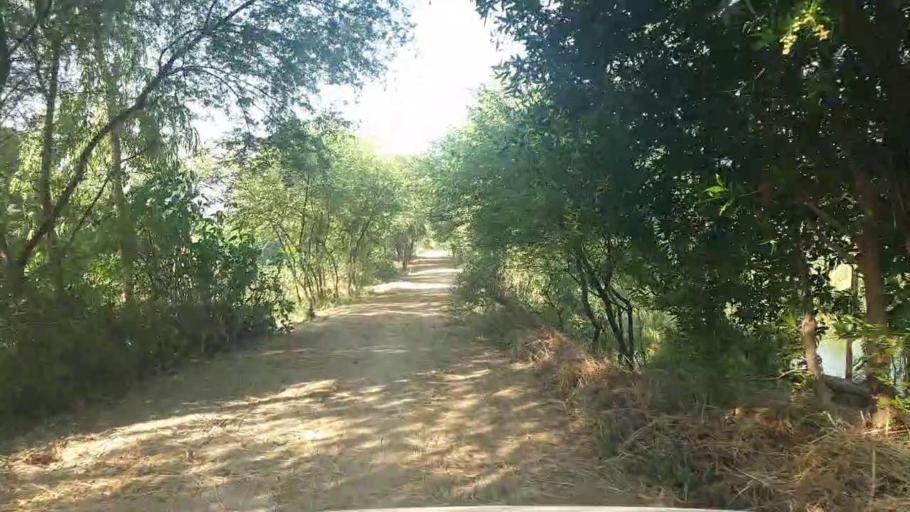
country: PK
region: Sindh
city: Badin
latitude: 24.7141
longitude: 68.9054
